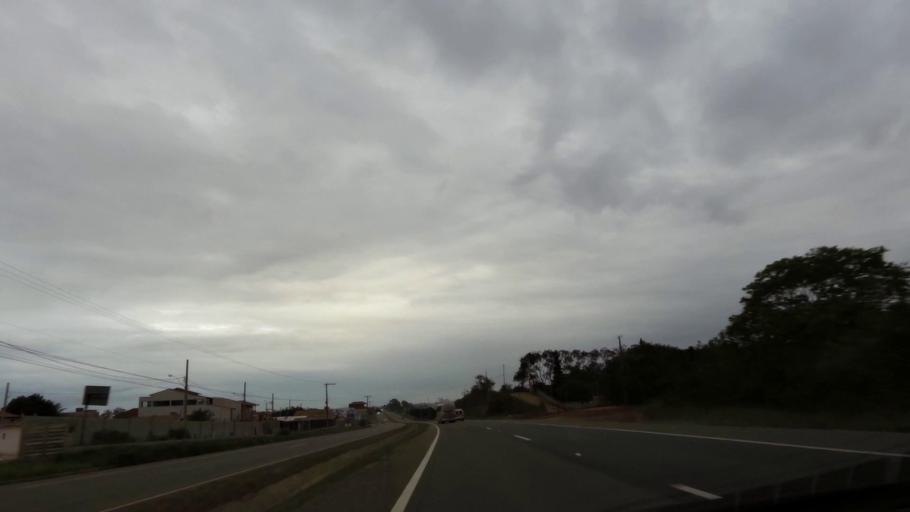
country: BR
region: Espirito Santo
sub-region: Guarapari
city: Guarapari
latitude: -20.5298
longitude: -40.3828
